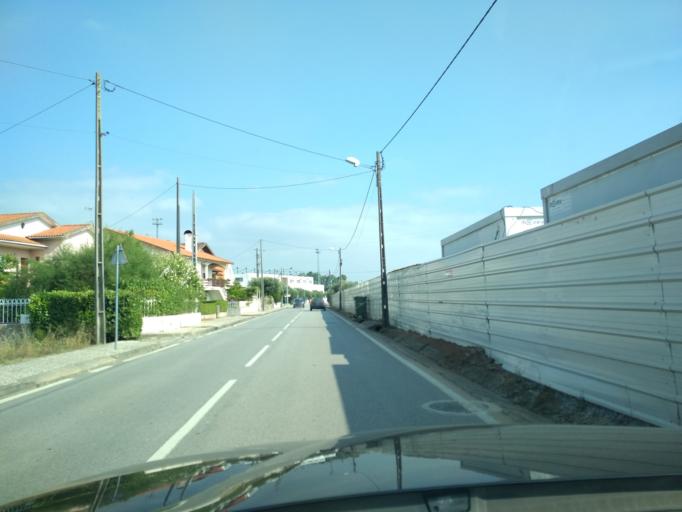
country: PT
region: Aveiro
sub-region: Mealhada
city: Mealhada
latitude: 40.3757
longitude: -8.4573
